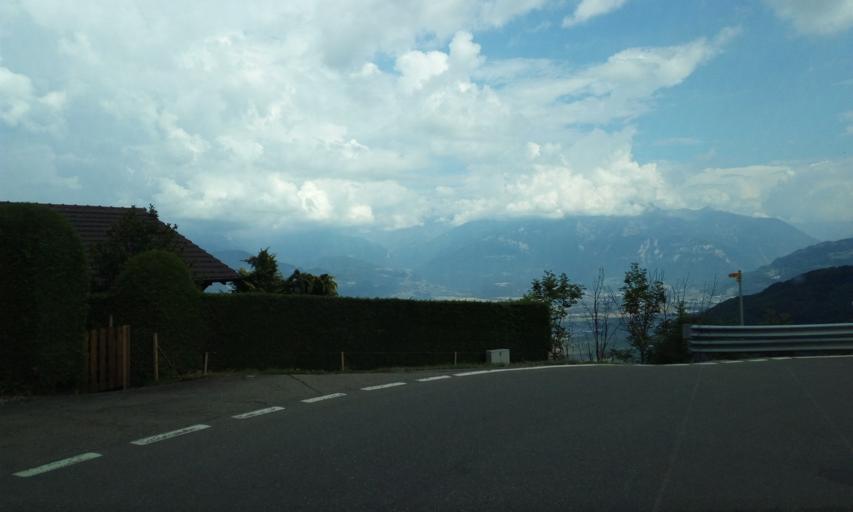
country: CH
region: Valais
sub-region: Monthey District
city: Vionnaz
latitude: 46.3155
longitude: 6.8796
